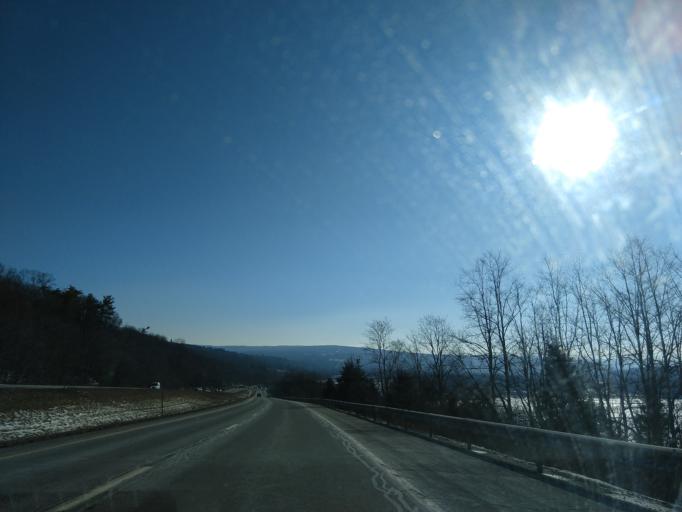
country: US
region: New York
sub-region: Tompkins County
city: Cayuga Heights
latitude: 42.4720
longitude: -76.5010
